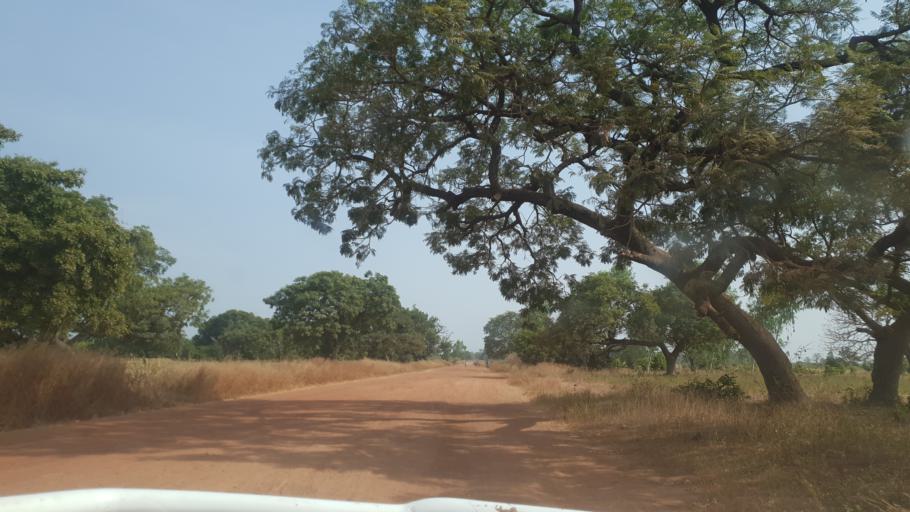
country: ML
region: Koulikoro
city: Dioila
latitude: 12.2266
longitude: -6.2160
